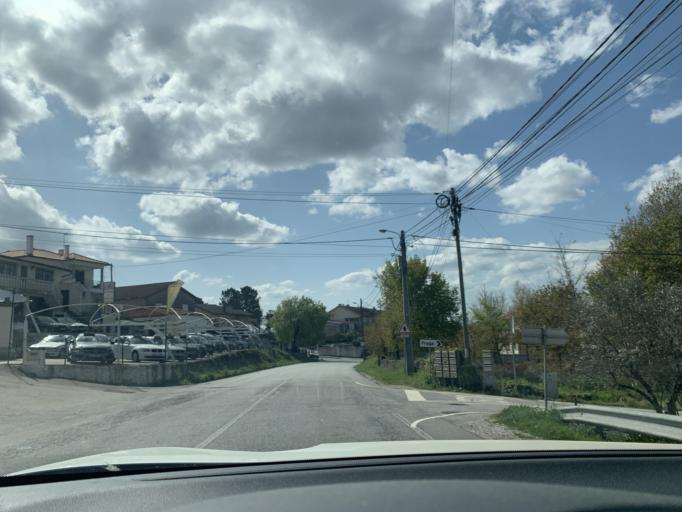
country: PT
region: Viseu
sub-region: Viseu
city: Rio de Loba
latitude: 40.6923
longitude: -7.8741
